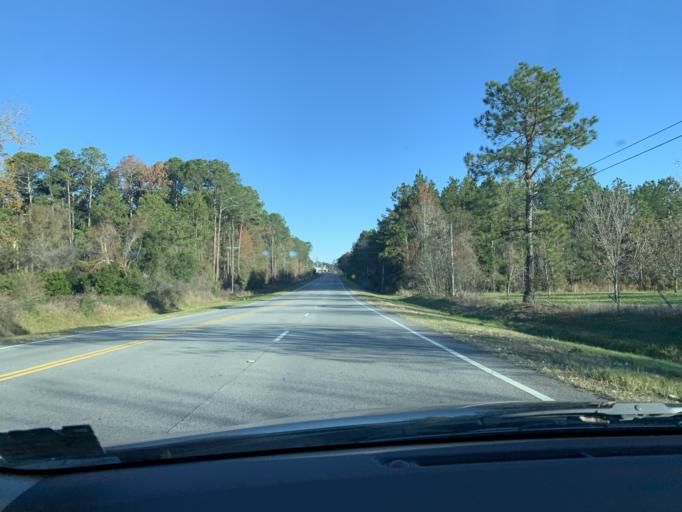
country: US
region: Georgia
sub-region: Irwin County
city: Ocilla
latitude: 31.6397
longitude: -83.2464
